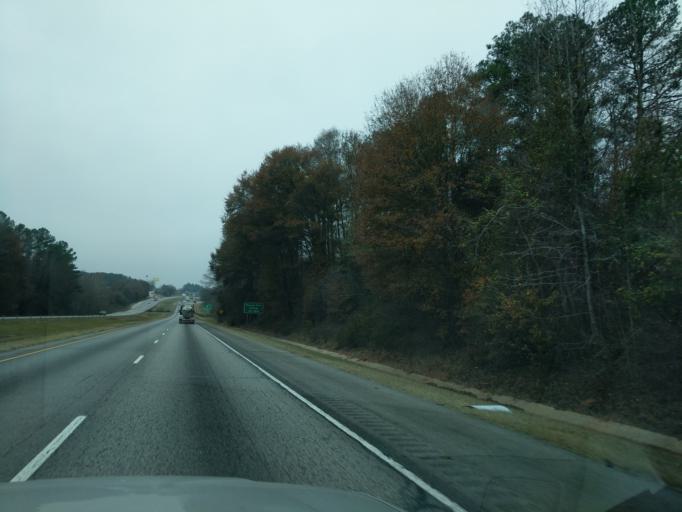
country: US
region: Georgia
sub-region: Franklin County
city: Carnesville
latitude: 34.3816
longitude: -83.2485
